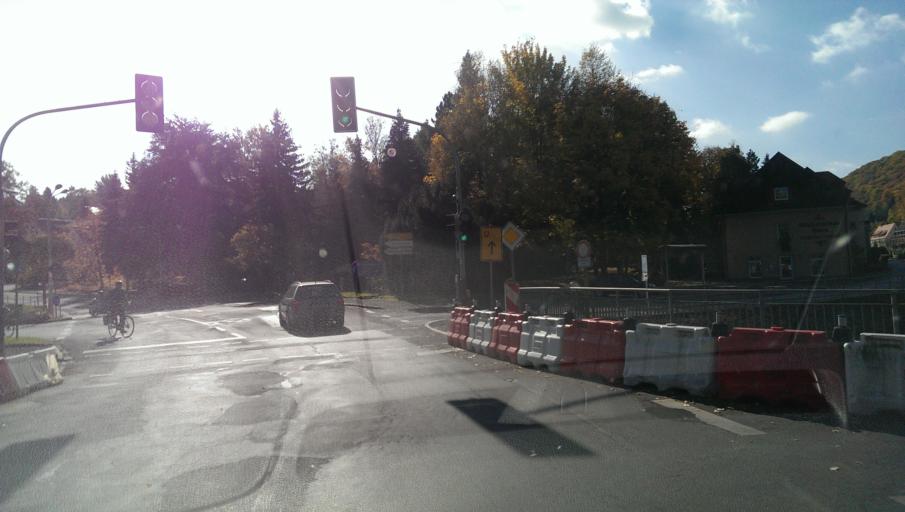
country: DE
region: Saxony
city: Dohma
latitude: 50.8754
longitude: 13.9479
